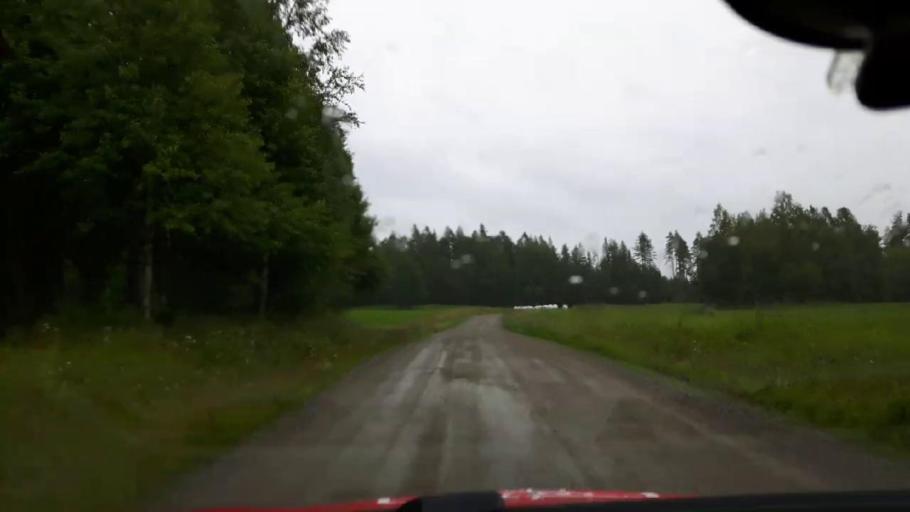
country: SE
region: Jaemtland
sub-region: OEstersunds Kommun
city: Brunflo
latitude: 62.8528
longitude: 14.9630
